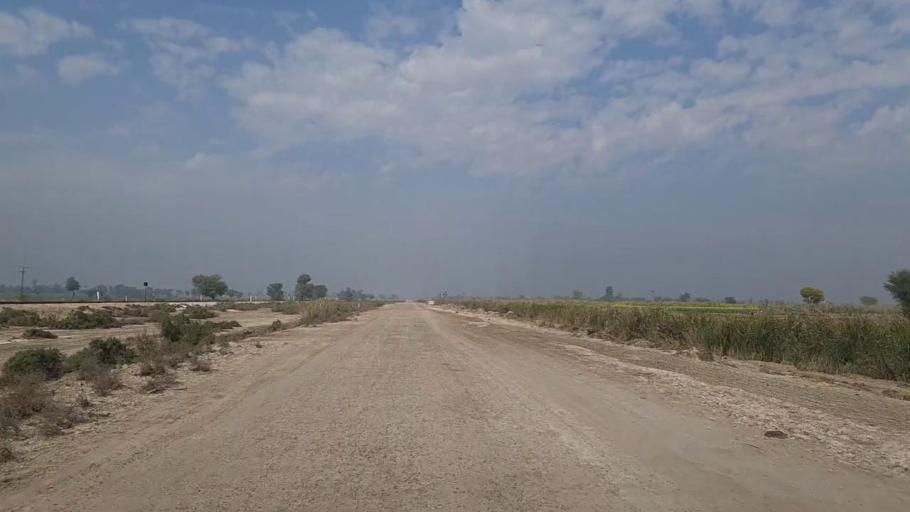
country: PK
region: Sindh
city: Daur
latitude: 26.3734
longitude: 68.3577
